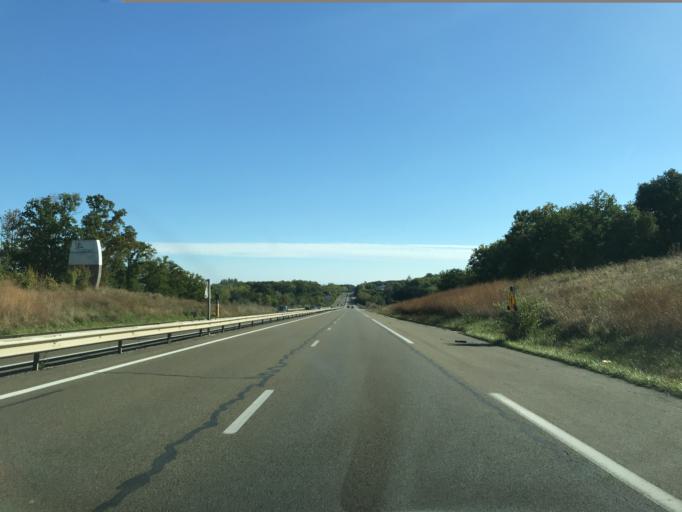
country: FR
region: Ile-de-France
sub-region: Departement de Seine-et-Marne
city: Quincy-Voisins
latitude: 48.9060
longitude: 2.8862
